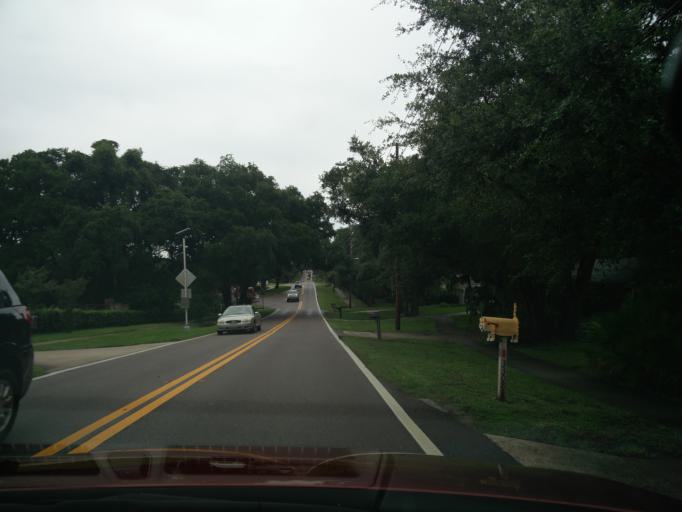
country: US
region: Florida
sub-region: Pinellas County
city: Safety Harbor
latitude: 28.0122
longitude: -82.6998
